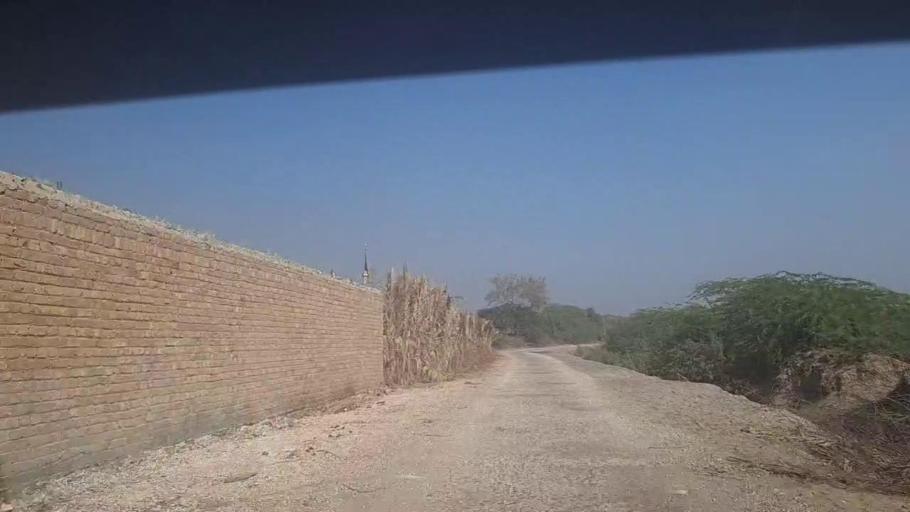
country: PK
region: Sindh
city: Khairpur
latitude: 27.4555
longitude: 68.7241
